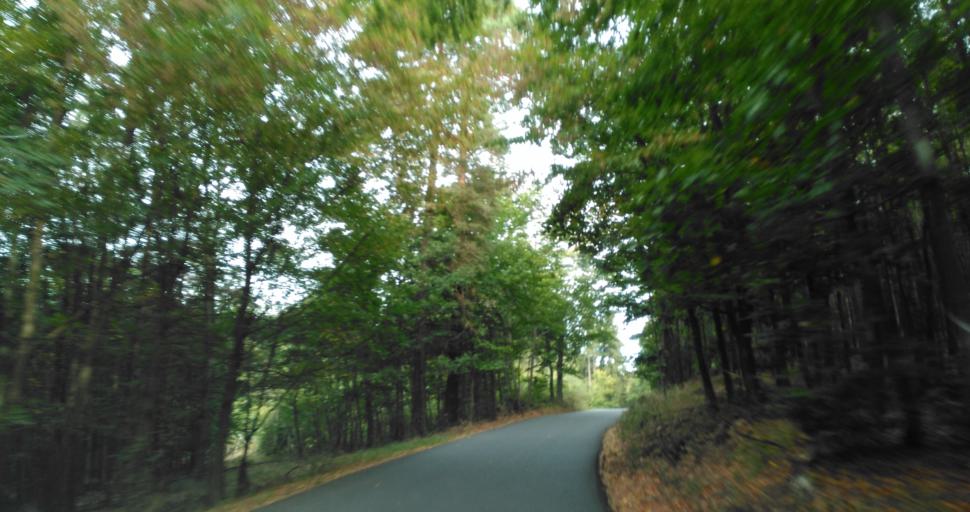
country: CZ
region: Plzensky
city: Zbiroh
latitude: 49.9340
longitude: 13.7782
